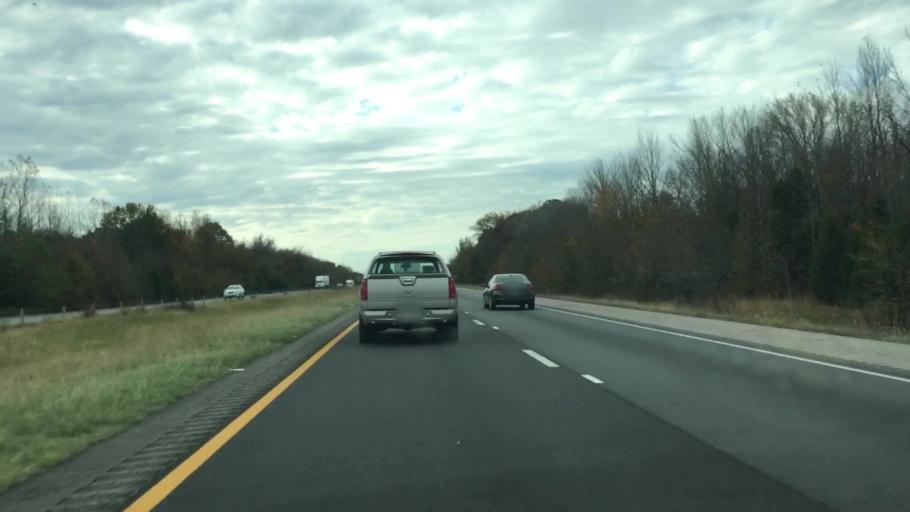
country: US
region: Arkansas
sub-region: Conway County
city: Morrilton
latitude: 35.1621
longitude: -92.6089
